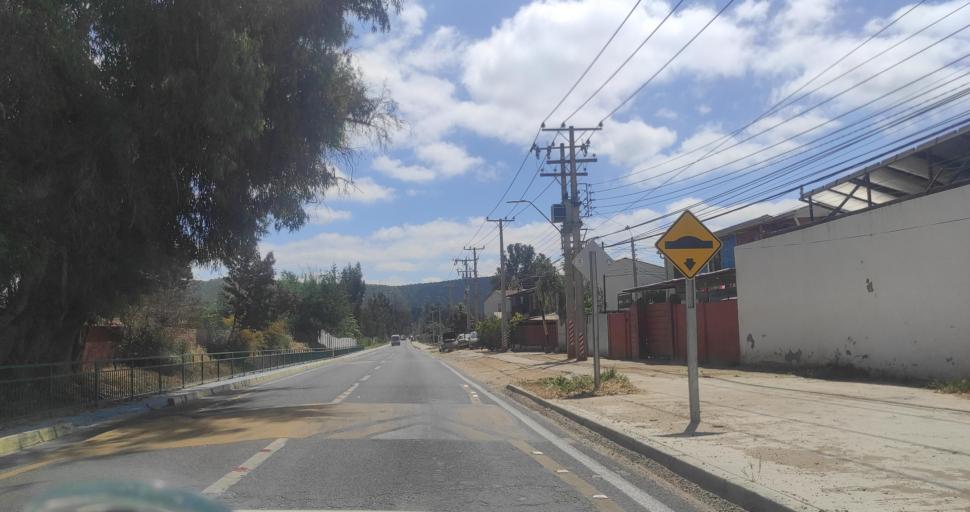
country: CL
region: Valparaiso
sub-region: Provincia de Marga Marga
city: Limache
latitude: -33.0213
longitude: -71.2636
